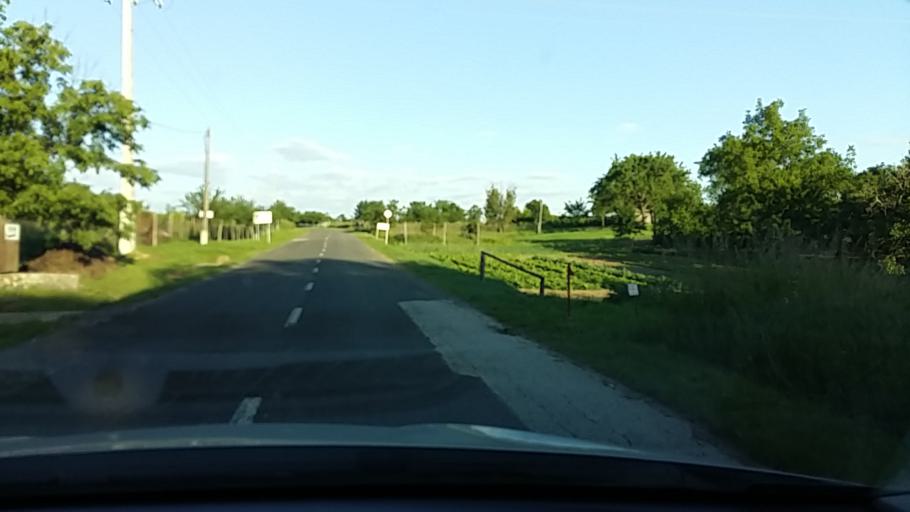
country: HU
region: Nograd
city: Diosjeno
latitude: 47.9079
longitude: 19.0564
